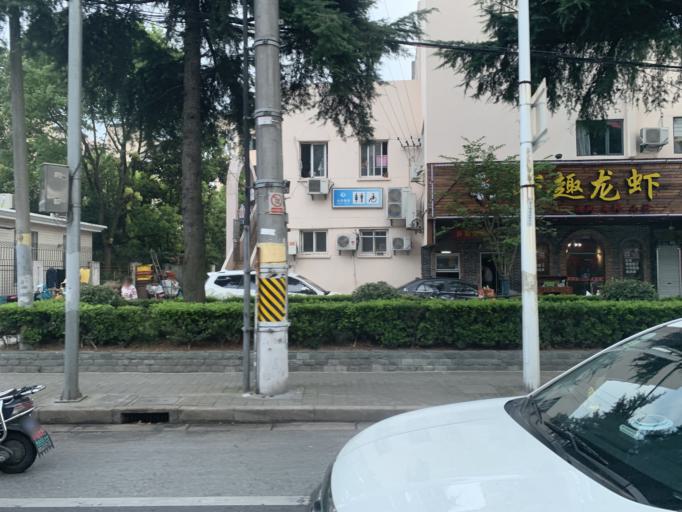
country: CN
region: Shanghai Shi
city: Pudong
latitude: 31.2366
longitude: 121.5228
